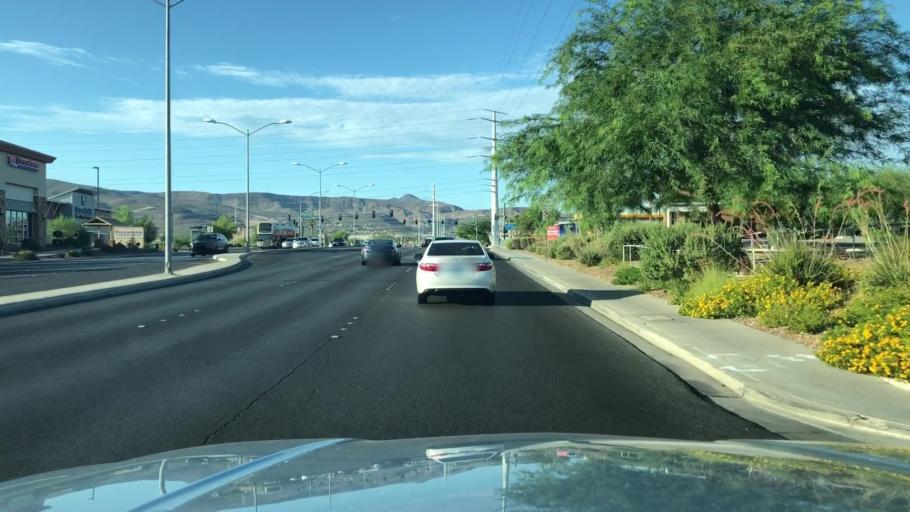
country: US
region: Nevada
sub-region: Clark County
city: Whitney
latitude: 36.0435
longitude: -115.0468
